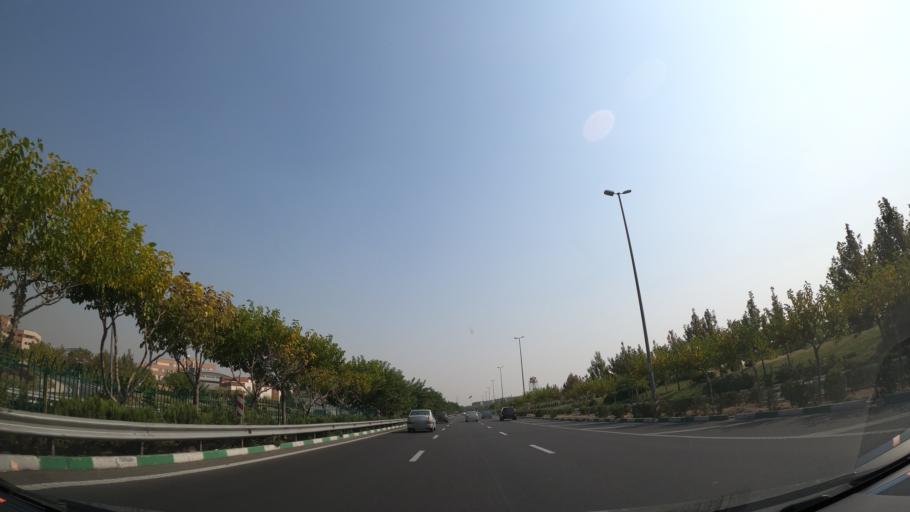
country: IR
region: Tehran
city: Shahr-e Qods
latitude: 35.7594
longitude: 51.2569
